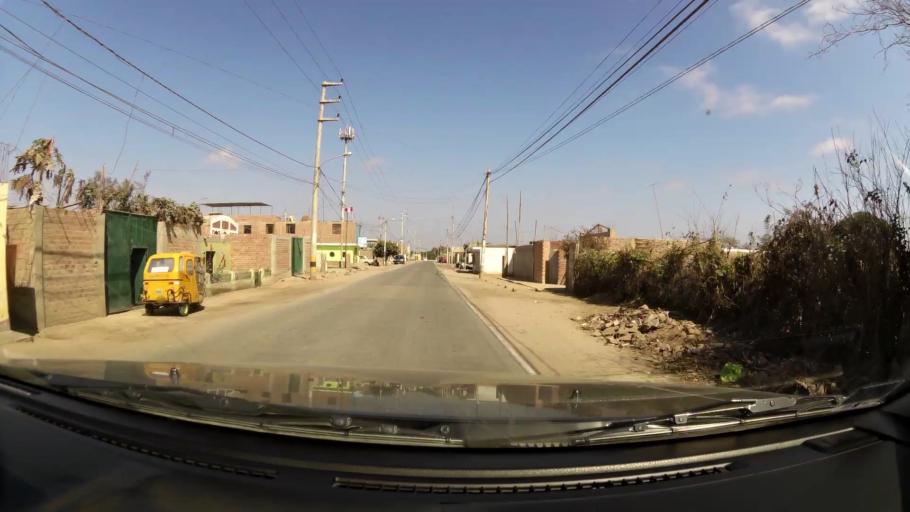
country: PE
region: Ica
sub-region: Provincia de Chincha
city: Sunampe
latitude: -13.4223
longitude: -76.1583
